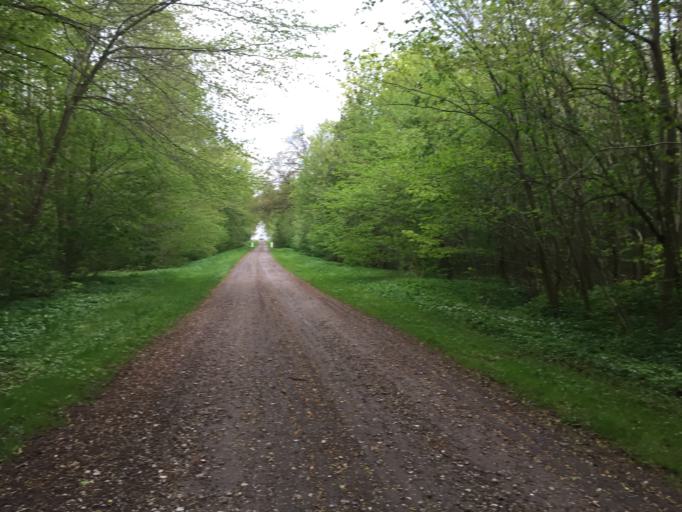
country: DK
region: North Denmark
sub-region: Alborg Kommune
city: Frejlev
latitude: 57.0050
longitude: 9.7798
